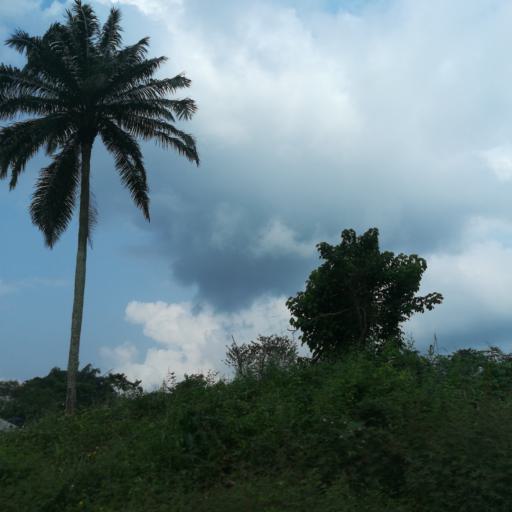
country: NG
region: Rivers
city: Okrika
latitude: 4.8314
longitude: 7.1267
